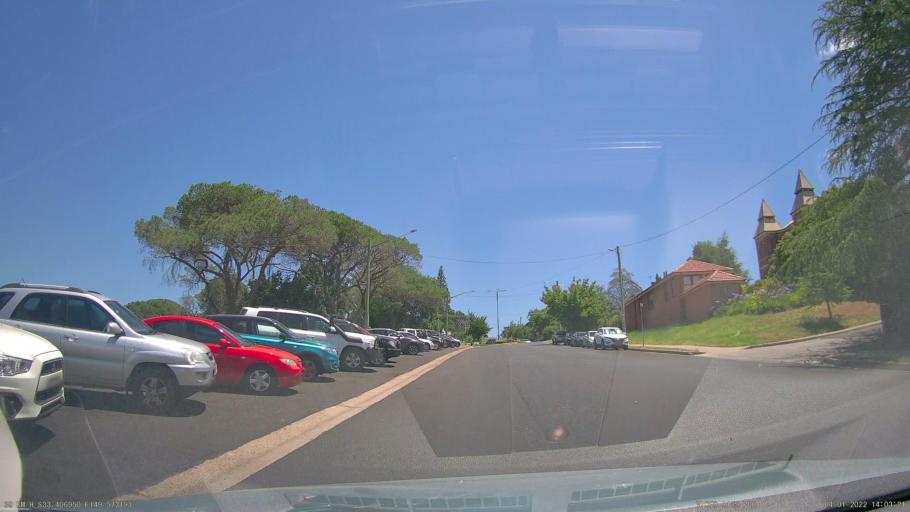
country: AU
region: New South Wales
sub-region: Bathurst Regional
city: Bathurst
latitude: -33.4070
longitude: 149.5731
